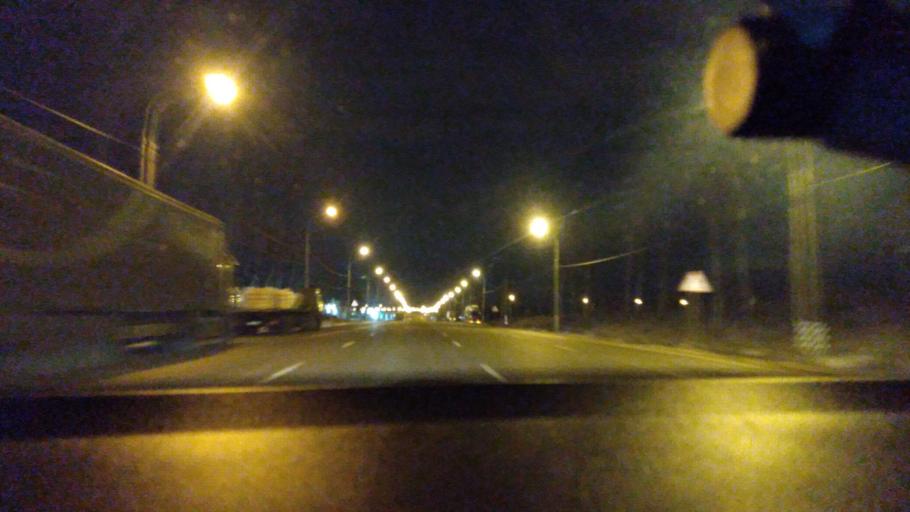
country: RU
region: Moskovskaya
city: Raduzhnyy
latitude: 55.1593
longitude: 38.6876
